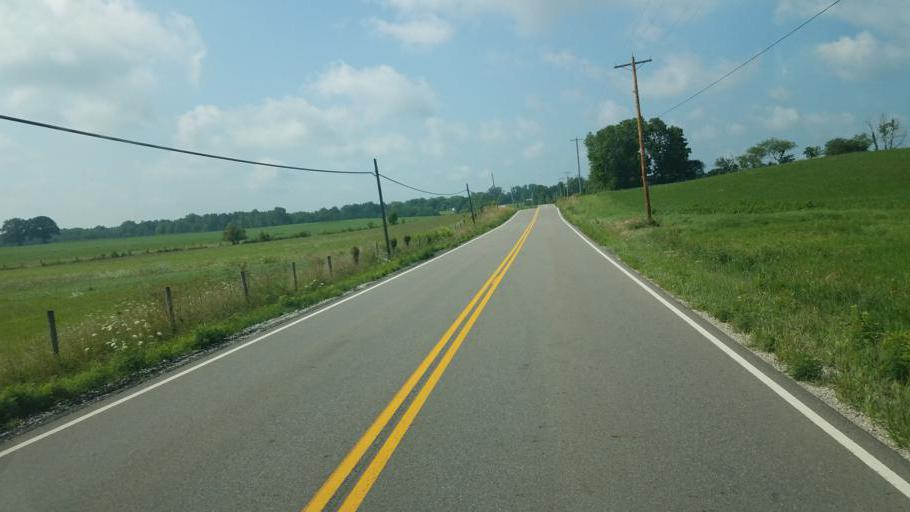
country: US
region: Ohio
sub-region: Knox County
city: Mount Vernon
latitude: 40.3402
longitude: -82.5059
